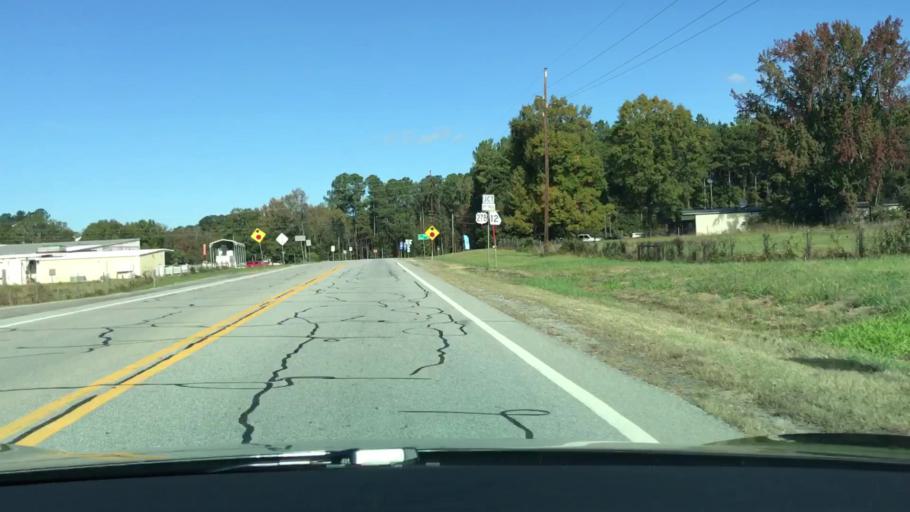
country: US
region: Georgia
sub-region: Warren County
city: Warrenton
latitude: 33.3996
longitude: -82.6548
